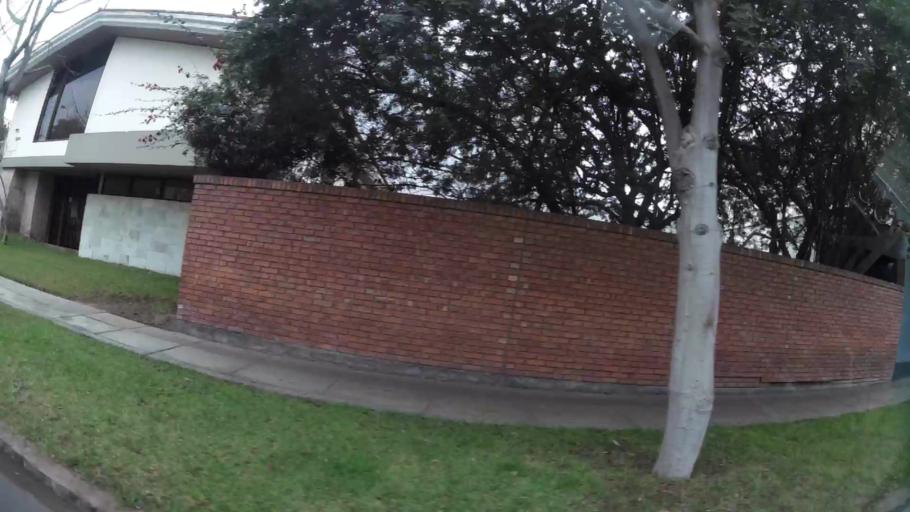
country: PE
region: Lima
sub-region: Lima
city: San Luis
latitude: -12.1095
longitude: -76.9841
